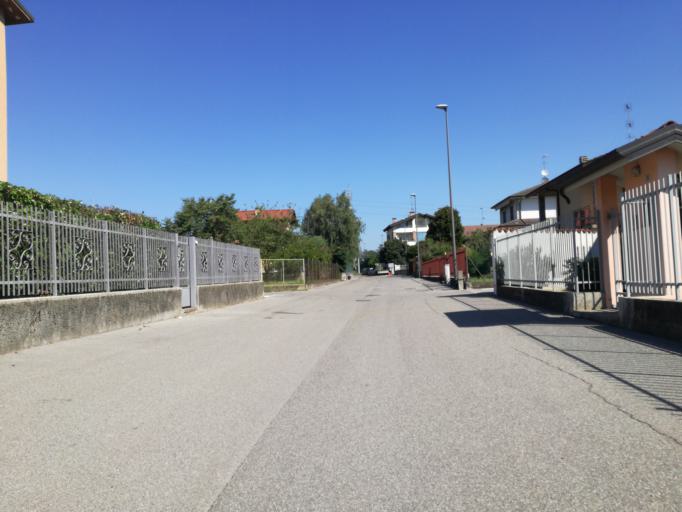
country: IT
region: Lombardy
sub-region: Provincia di Monza e Brianza
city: Porto d'Adda
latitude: 45.6647
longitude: 9.4786
